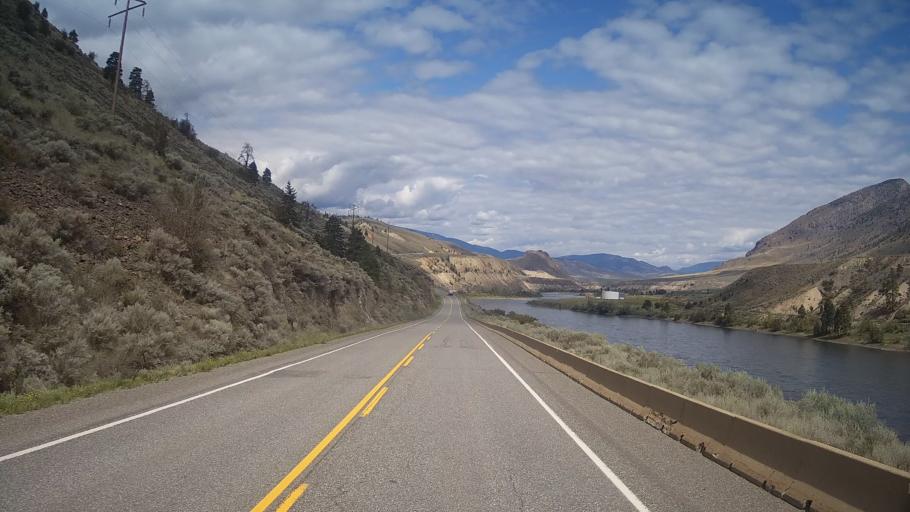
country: CA
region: British Columbia
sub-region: Thompson-Nicola Regional District
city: Ashcroft
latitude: 50.5456
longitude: -121.2919
